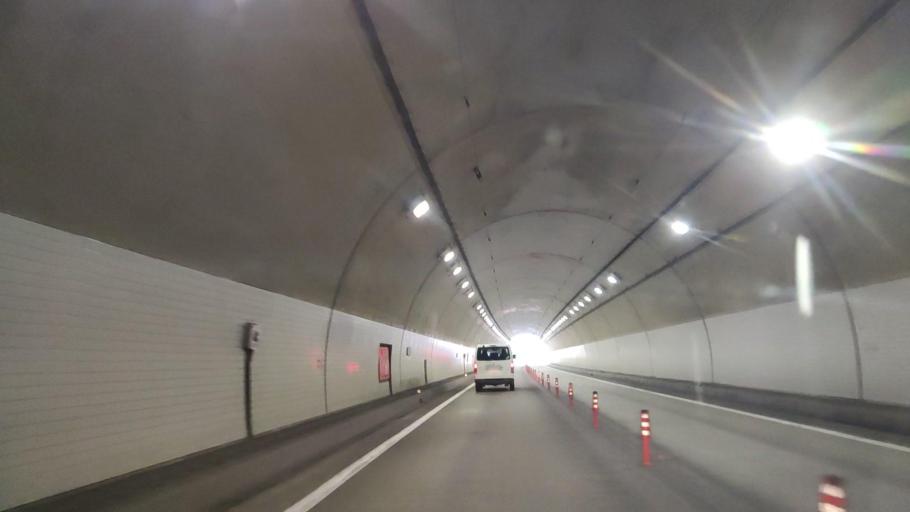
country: JP
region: Akita
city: Odate
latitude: 40.3459
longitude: 140.6647
